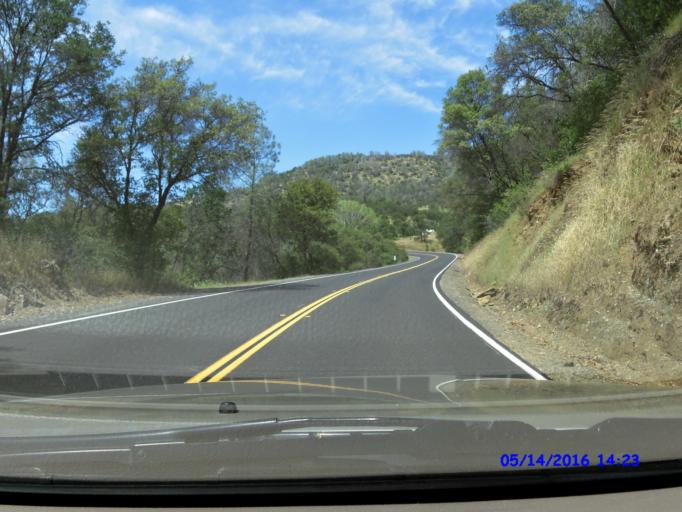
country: US
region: California
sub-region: Tuolumne County
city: Tuolumne City
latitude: 37.6912
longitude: -120.1814
